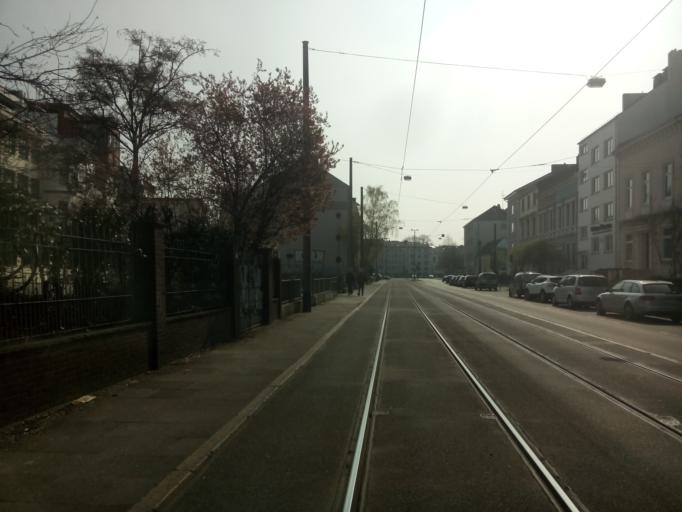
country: DE
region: Bremen
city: Bremen
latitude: 53.0793
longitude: 8.8215
